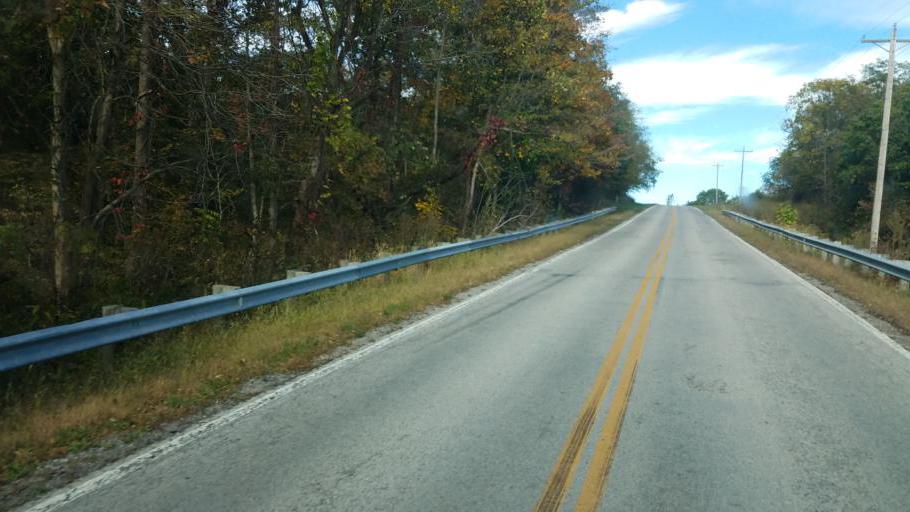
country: US
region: Ohio
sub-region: Huron County
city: Greenwich
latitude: 41.1026
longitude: -82.4869
